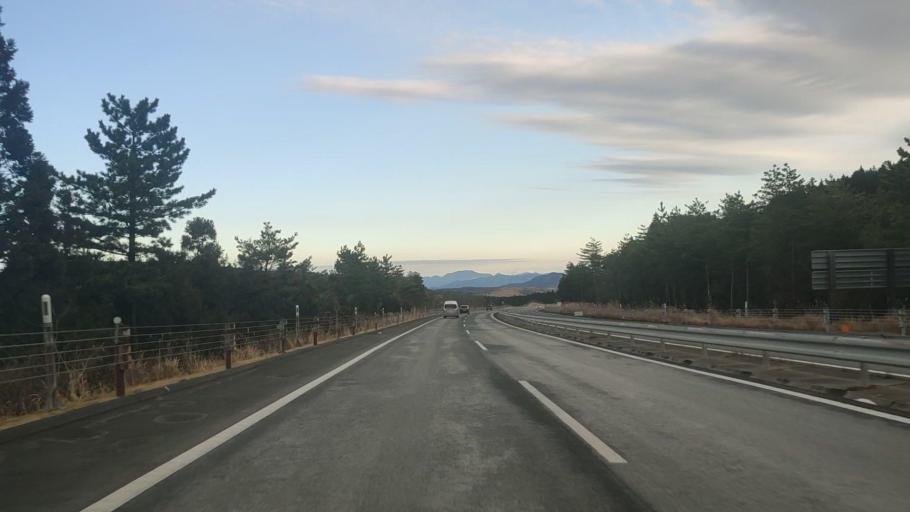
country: JP
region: Oita
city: Beppu
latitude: 33.3251
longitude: 131.4159
